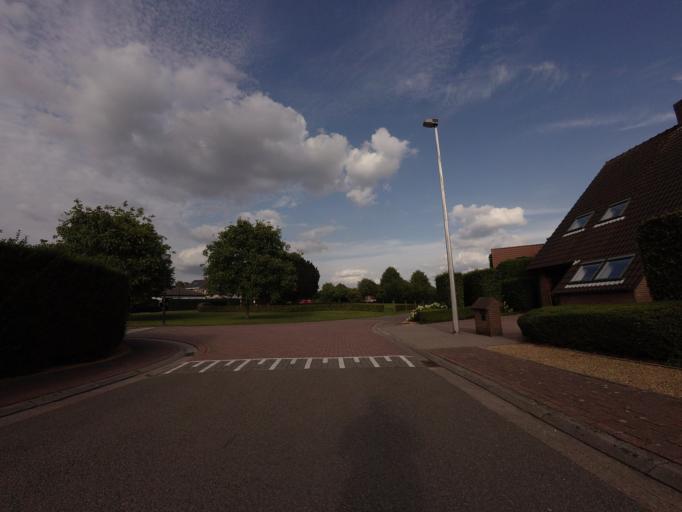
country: BE
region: Flanders
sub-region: Provincie Vlaams-Brabant
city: Meise
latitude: 50.9406
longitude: 4.3382
